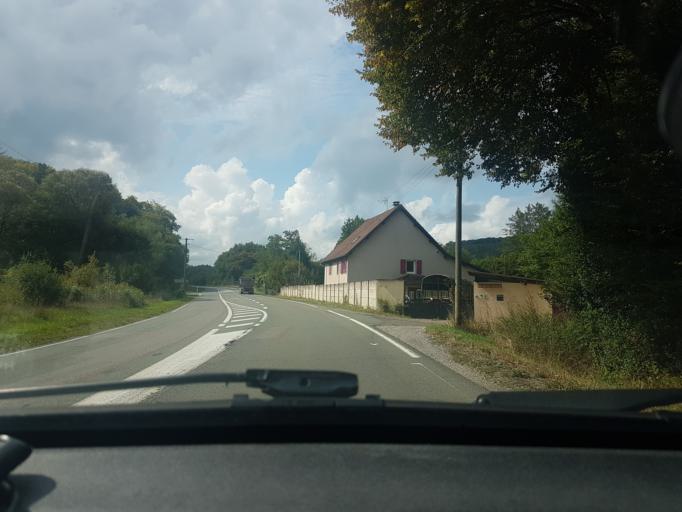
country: FR
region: Franche-Comte
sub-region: Departement de la Haute-Saone
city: Hericourt
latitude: 47.5930
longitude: 6.7108
